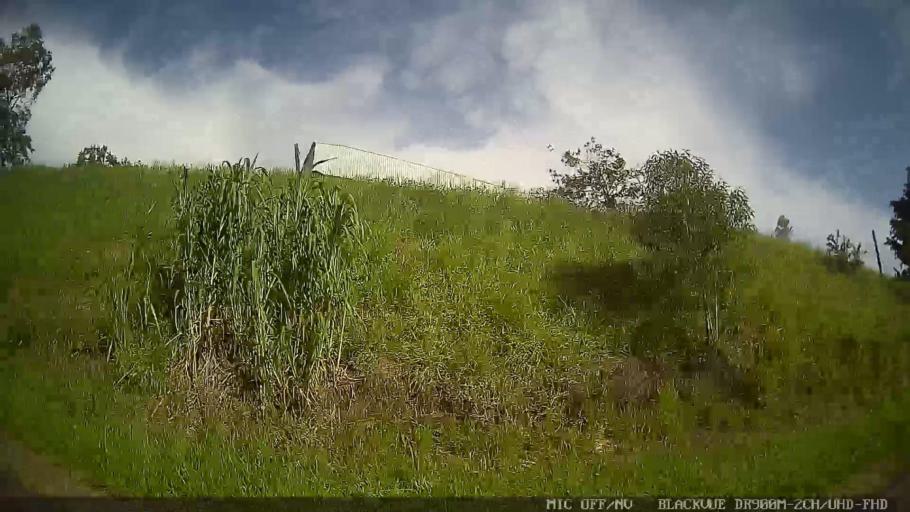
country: BR
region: Sao Paulo
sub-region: Tiete
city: Tiete
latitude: -23.0959
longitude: -47.6880
